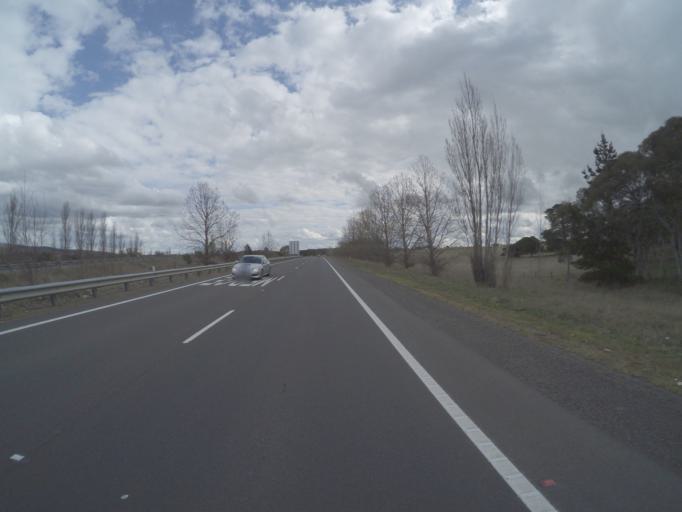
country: AU
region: New South Wales
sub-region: Goulburn Mulwaree
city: Goulburn
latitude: -34.8010
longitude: 149.6105
